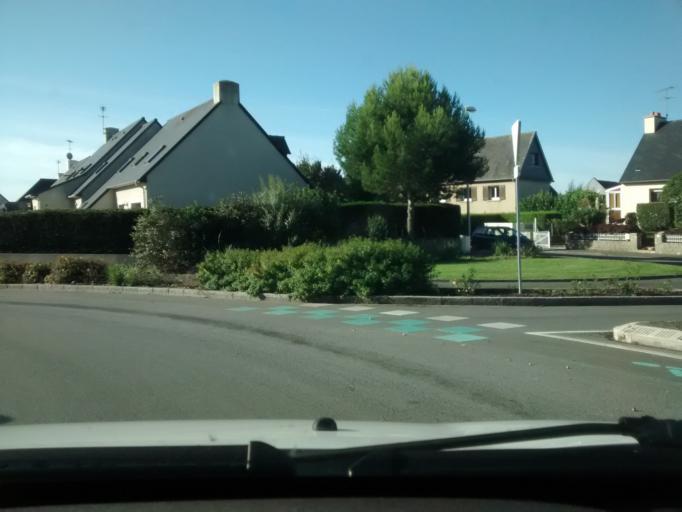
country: FR
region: Brittany
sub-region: Departement d'Ille-et-Vilaine
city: Saint-Malo
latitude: 48.6526
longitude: -1.9733
